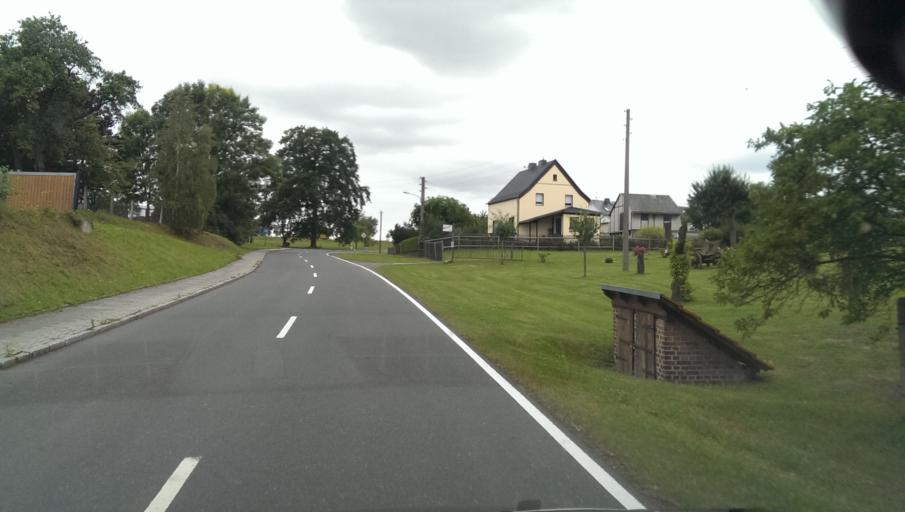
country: DE
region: Thuringia
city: Langenwolschendorf
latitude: 50.6480
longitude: 11.9462
